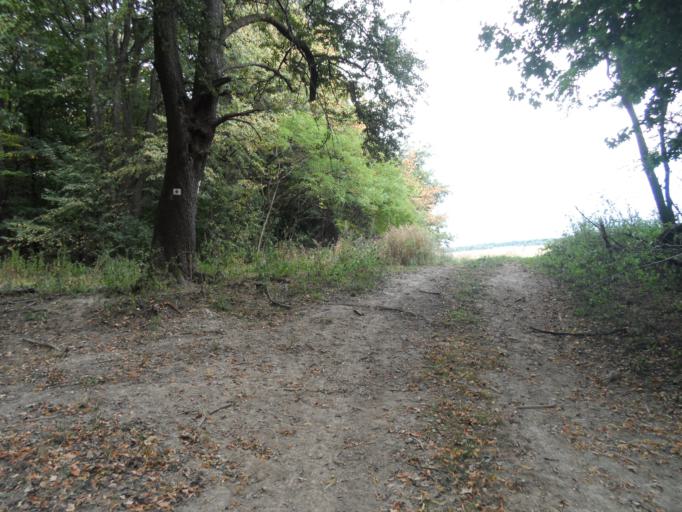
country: HU
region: Veszprem
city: Ajka
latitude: 47.1862
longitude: 17.6054
